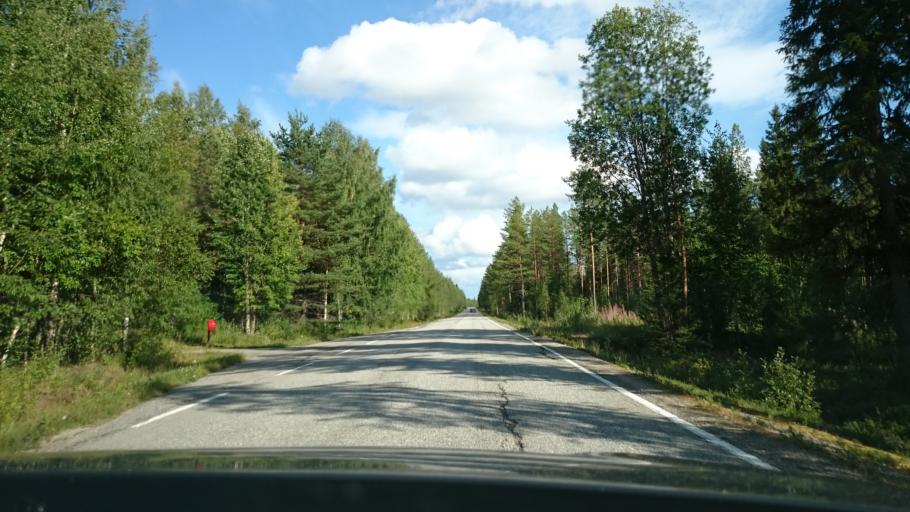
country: FI
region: Kainuu
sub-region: Kehys-Kainuu
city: Suomussalmi
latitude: 64.7574
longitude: 29.3954
